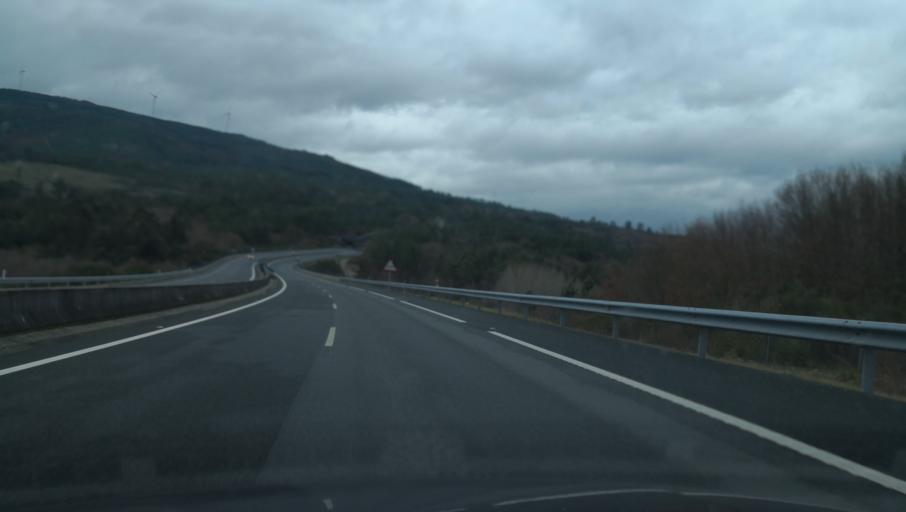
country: ES
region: Galicia
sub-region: Provincia de Ourense
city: Pinor
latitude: 42.4933
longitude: -8.0255
